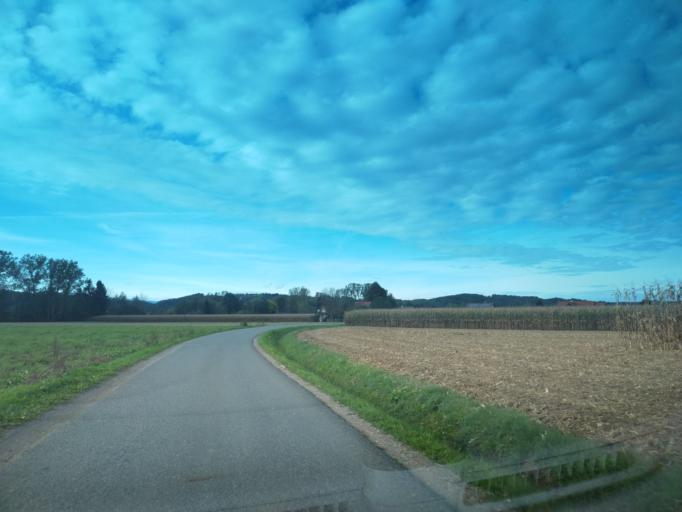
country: AT
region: Styria
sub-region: Politischer Bezirk Leibnitz
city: Sankt Johann im Saggautal
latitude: 46.6919
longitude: 15.3941
